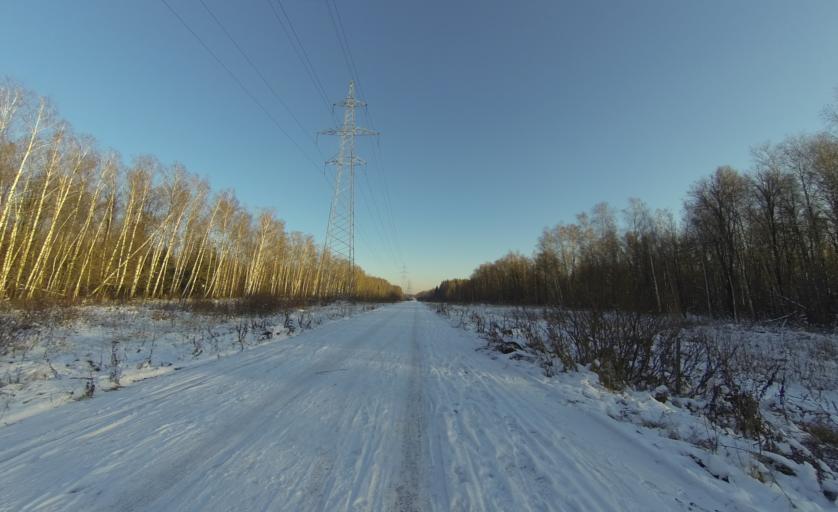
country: RU
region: Moscow
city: Babushkin
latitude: 55.8425
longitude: 37.7321
